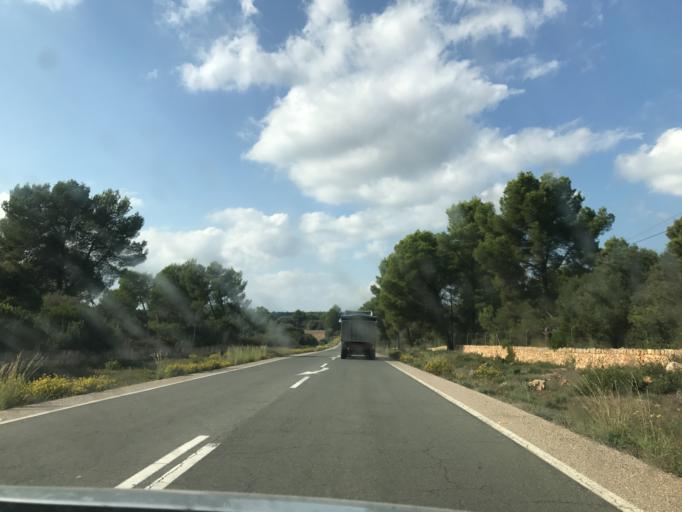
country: ES
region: Balearic Islands
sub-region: Illes Balears
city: Santa Margalida
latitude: 39.7251
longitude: 3.2069
